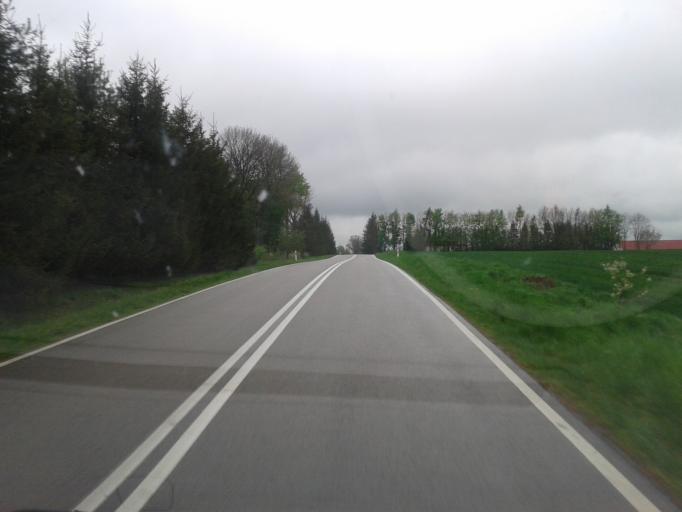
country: PL
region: Lublin Voivodeship
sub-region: Powiat tomaszowski
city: Telatyn
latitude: 50.5418
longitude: 23.9237
